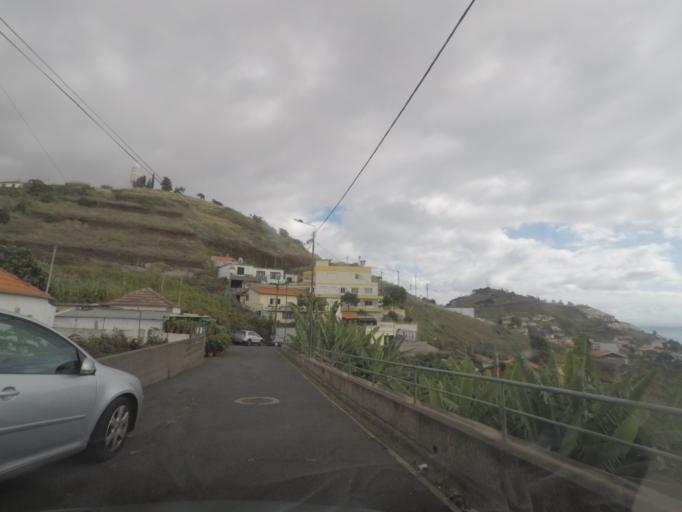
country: PT
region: Madeira
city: Camara de Lobos
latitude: 32.6485
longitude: -16.9473
